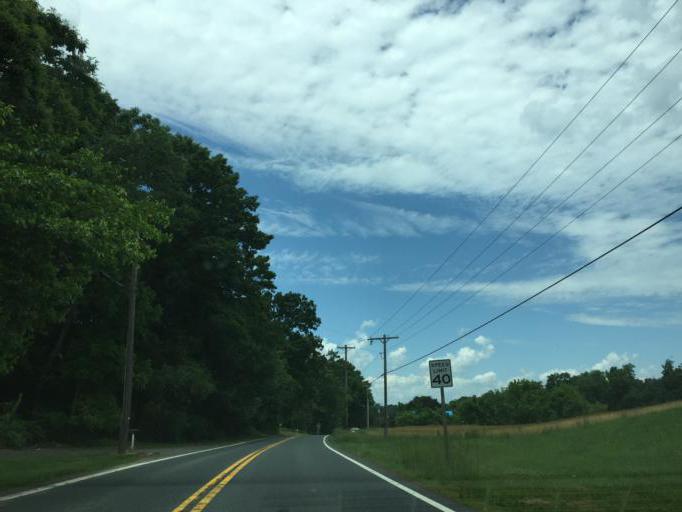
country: US
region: Pennsylvania
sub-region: York County
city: Susquehanna Trails
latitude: 39.6799
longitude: -76.3704
